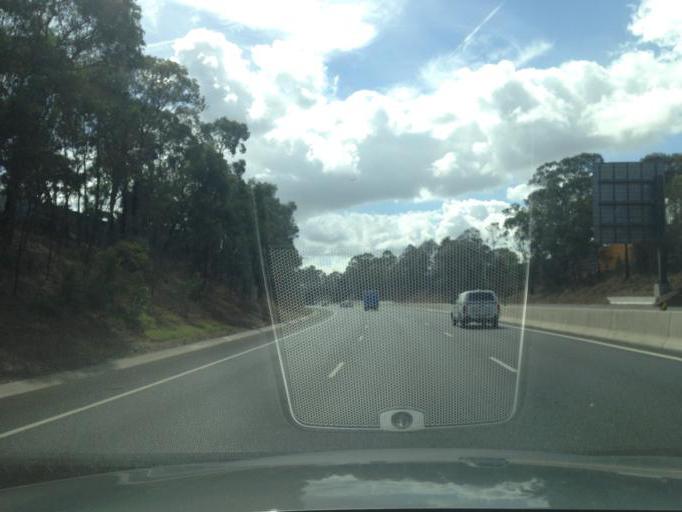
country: AU
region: New South Wales
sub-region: Bankstown
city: Milperra
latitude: -33.9435
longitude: 150.9972
